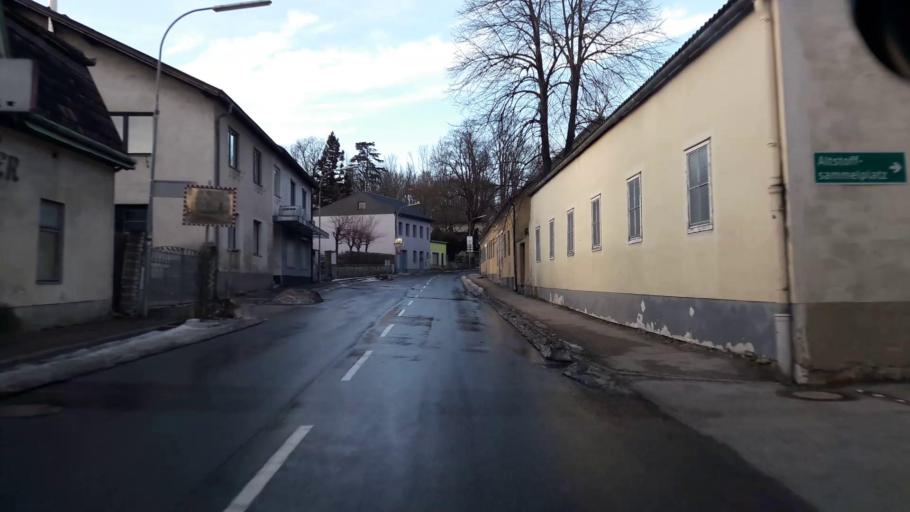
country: AT
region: Lower Austria
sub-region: Politischer Bezirk Wien-Umgebung
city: Mauerbach
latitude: 48.2463
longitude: 16.1670
